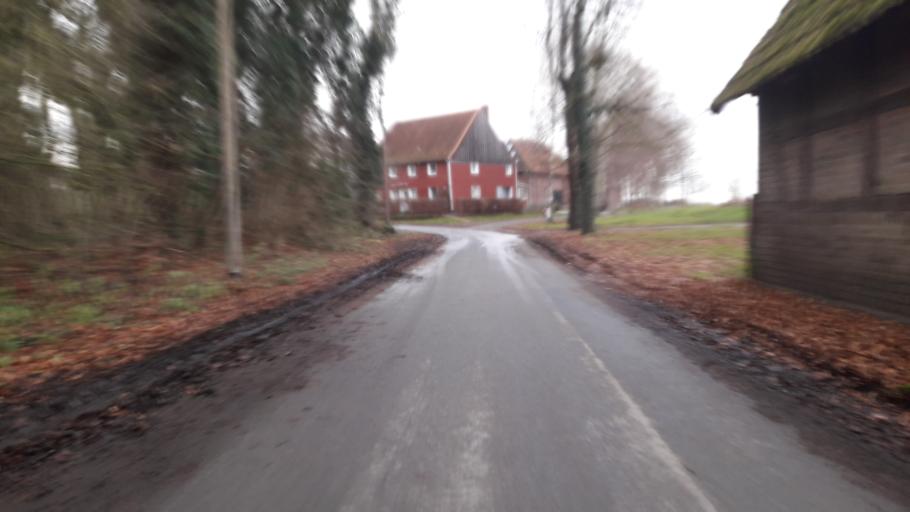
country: DE
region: North Rhine-Westphalia
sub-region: Regierungsbezirk Arnsberg
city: Welver
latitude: 51.5735
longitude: 8.0028
